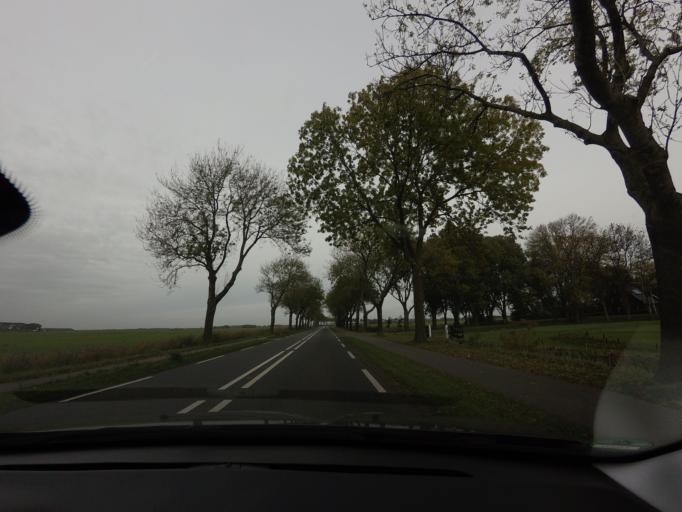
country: NL
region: Overijssel
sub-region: Gemeente Steenwijkerland
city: Blokzijl
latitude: 52.7306
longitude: 5.9580
